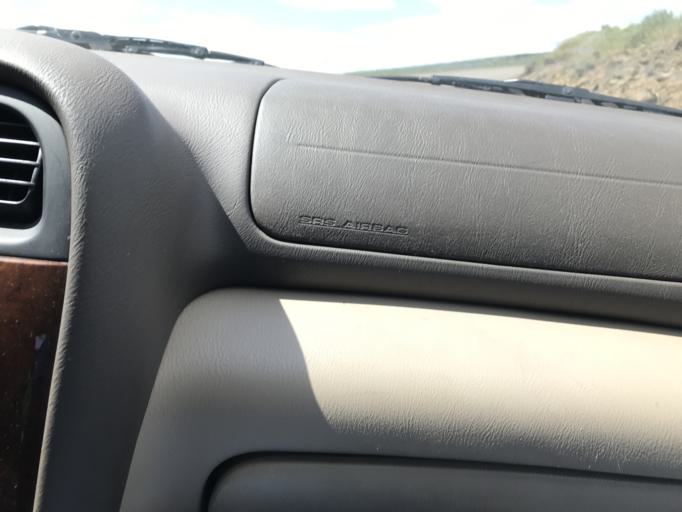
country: US
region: Washington
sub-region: Grant County
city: Quincy
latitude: 47.3081
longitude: -119.8250
